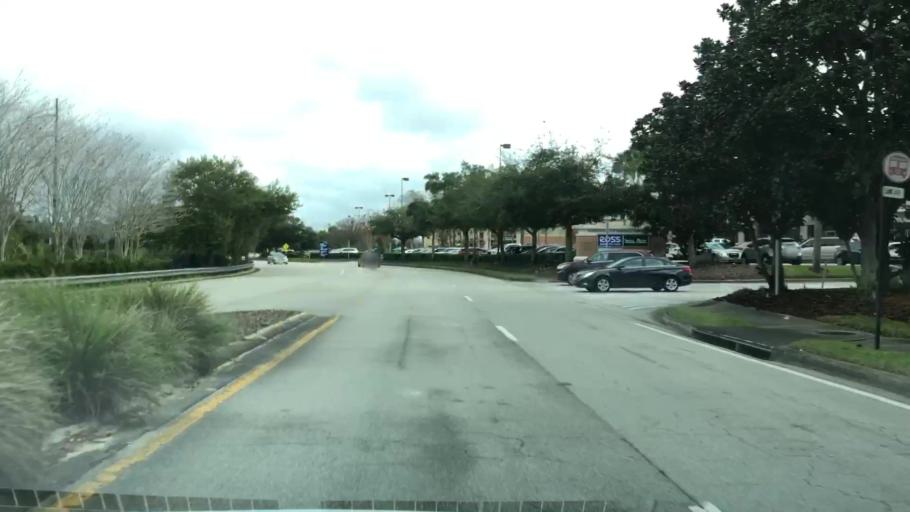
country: US
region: Florida
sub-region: Seminole County
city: Lake Mary
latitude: 28.8001
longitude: -81.3363
